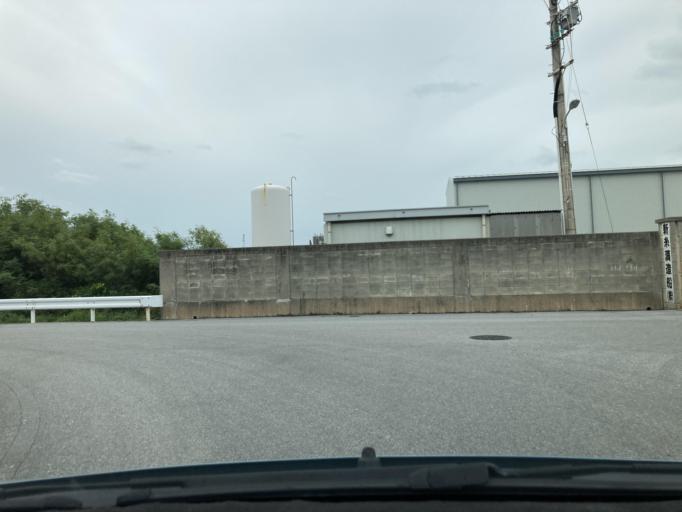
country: JP
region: Okinawa
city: Itoman
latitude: 26.1300
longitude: 127.6542
